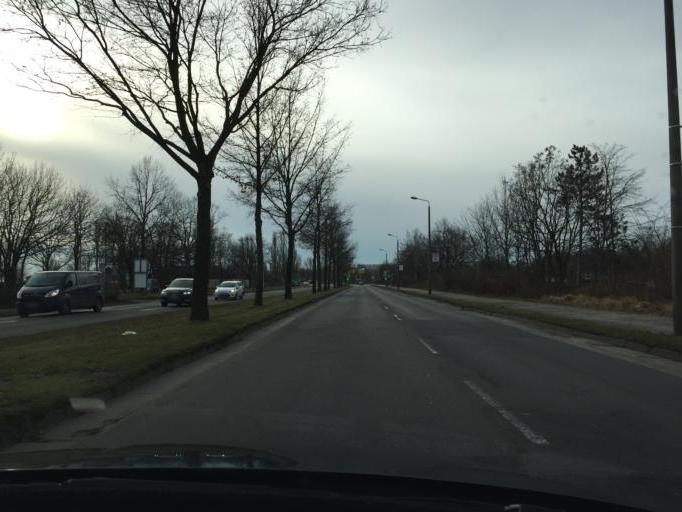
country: DE
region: Brandenburg
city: Cottbus
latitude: 51.7718
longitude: 14.3600
